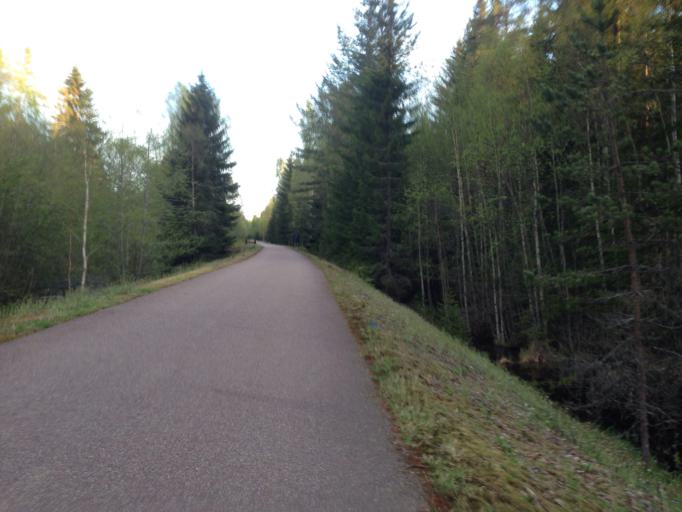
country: SE
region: Dalarna
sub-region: Ludvika Kommun
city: Grangesberg
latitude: 60.1322
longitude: 15.0705
